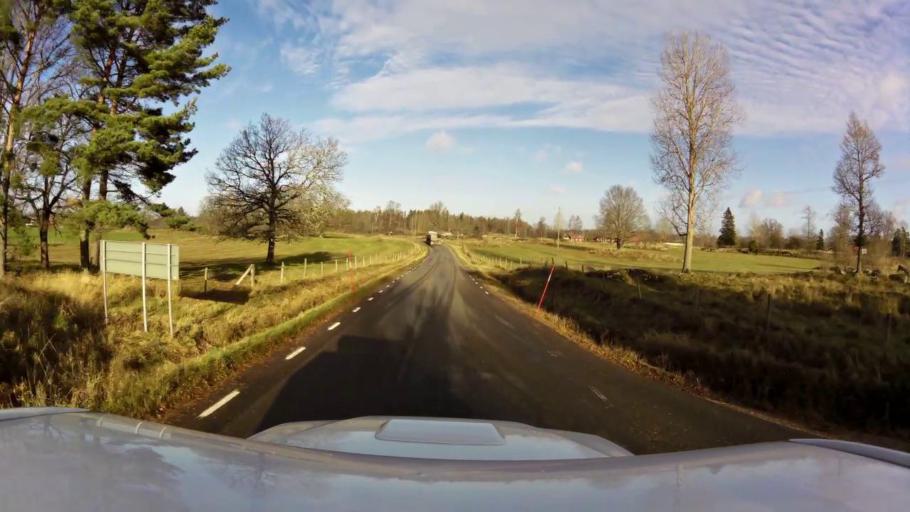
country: SE
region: OEstergoetland
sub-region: Linkopings Kommun
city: Linkoping
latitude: 58.3375
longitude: 15.6525
